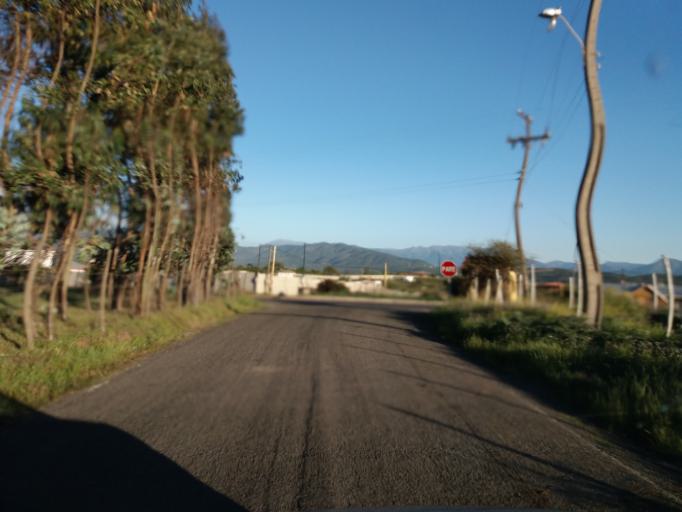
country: CL
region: Valparaiso
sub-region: Provincia de Quillota
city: Quillota
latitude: -32.9168
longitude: -71.3326
